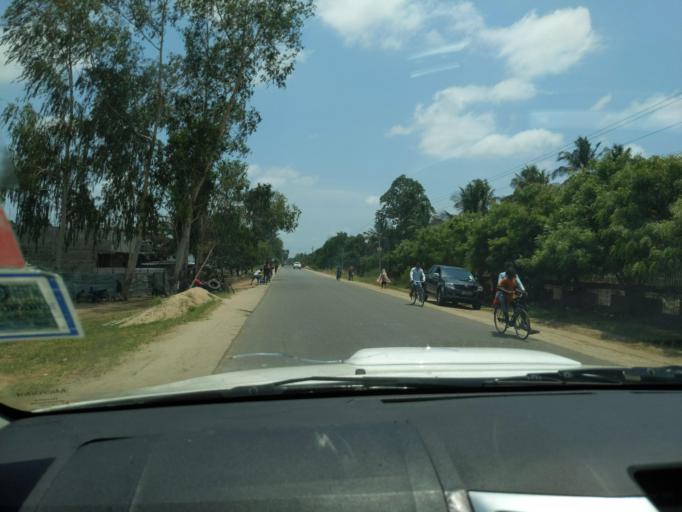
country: MZ
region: Zambezia
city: Quelimane
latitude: -17.8395
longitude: 36.9171
